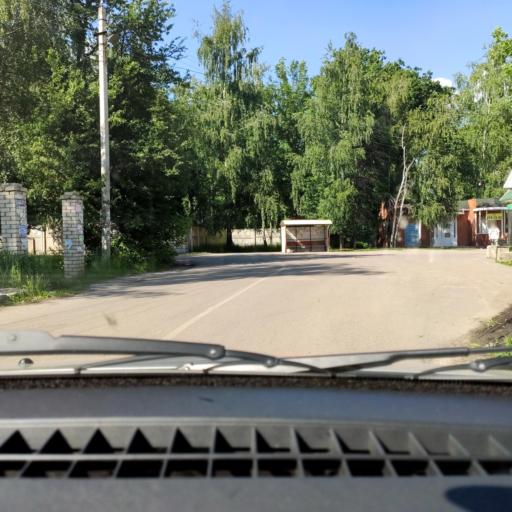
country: RU
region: Voronezj
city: Ramon'
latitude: 51.8213
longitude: 39.2666
